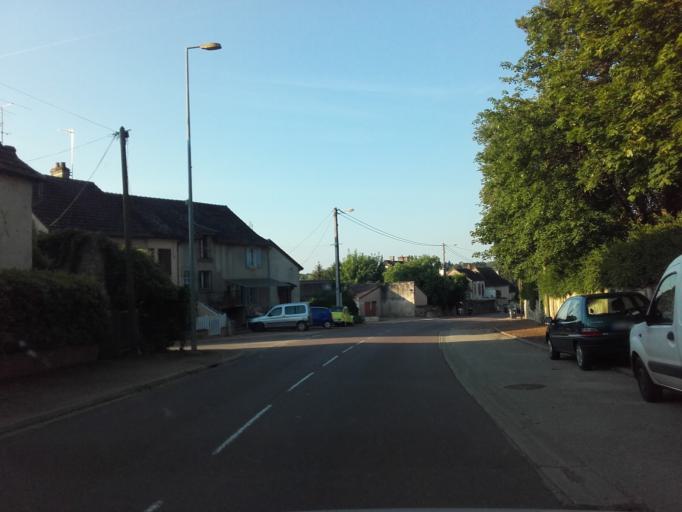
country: FR
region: Bourgogne
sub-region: Departement de Saone-et-Loire
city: Dracy-le-Fort
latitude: 46.8093
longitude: 4.7534
